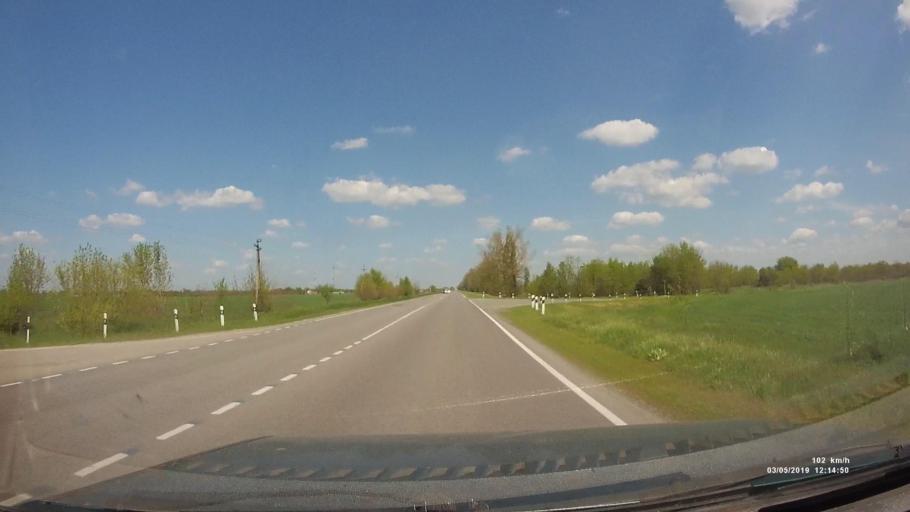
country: RU
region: Rostov
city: Melikhovskaya
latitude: 47.3495
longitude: 40.5675
